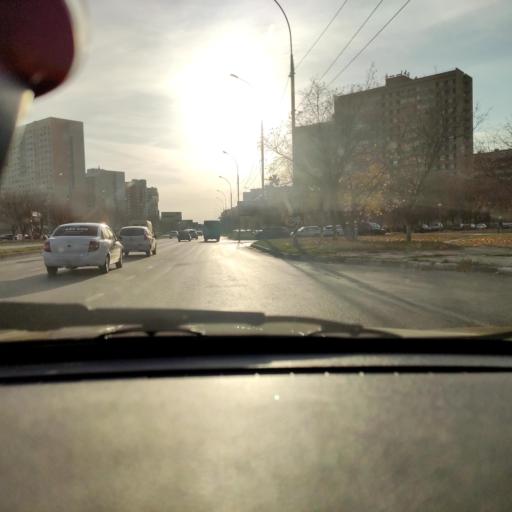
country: RU
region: Samara
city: Tol'yatti
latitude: 53.5315
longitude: 49.3415
